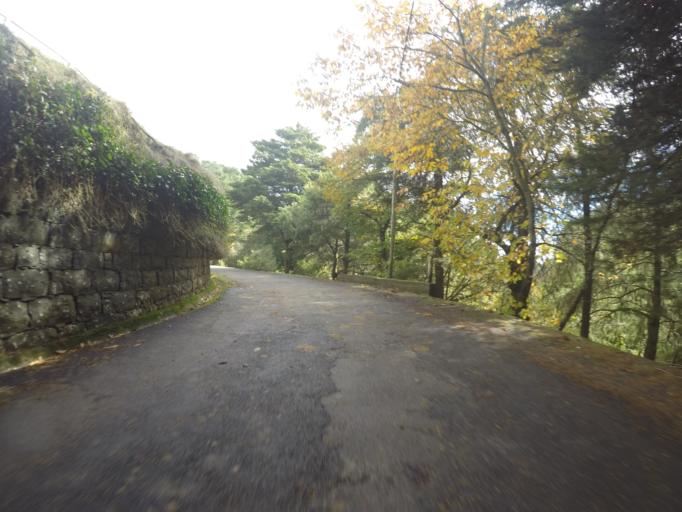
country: PT
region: Madeira
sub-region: Funchal
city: Nossa Senhora do Monte
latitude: 32.7033
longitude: -16.8887
